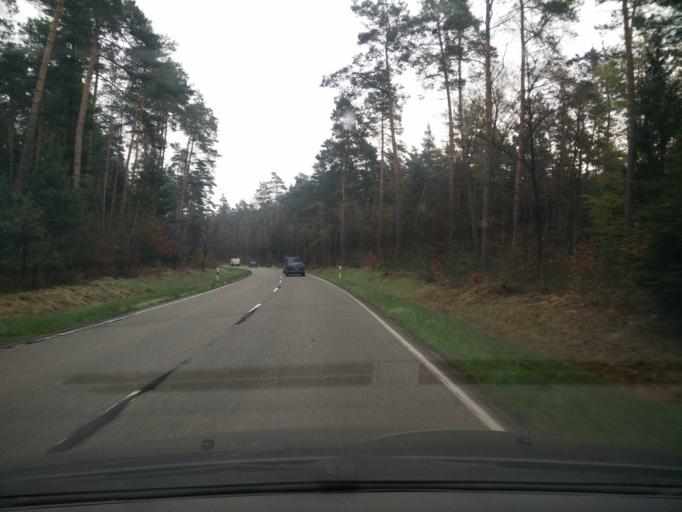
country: DE
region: Rheinland-Pfalz
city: Freckenfeld
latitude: 49.0454
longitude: 8.1001
